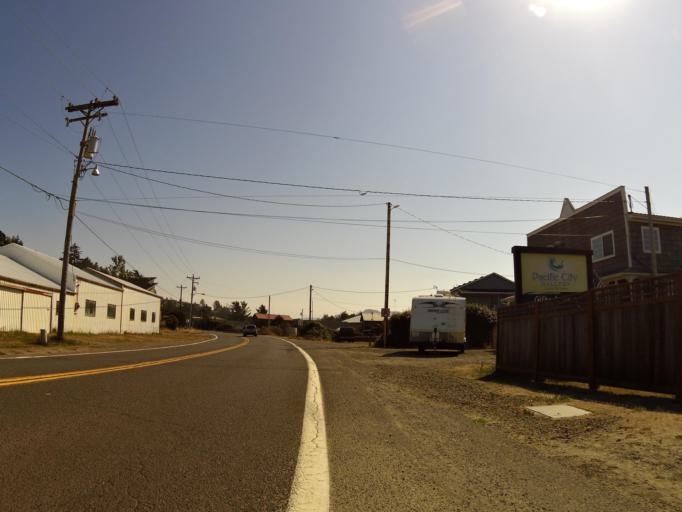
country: US
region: Oregon
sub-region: Tillamook County
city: Pacific City
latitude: 45.1994
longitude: -123.9611
